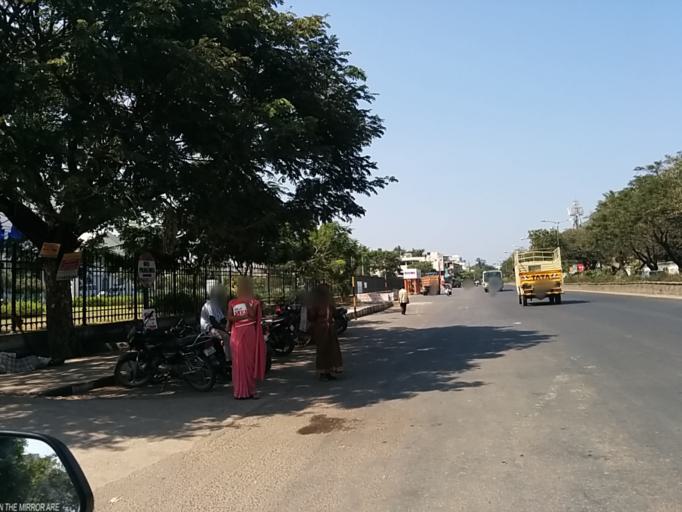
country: IN
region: Pondicherry
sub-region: Puducherry
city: Puducherry
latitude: 11.9368
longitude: 79.8079
